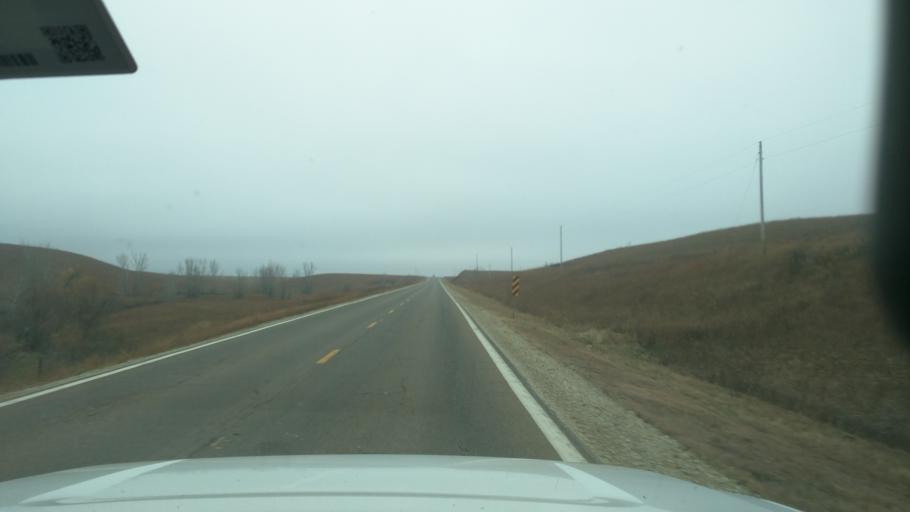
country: US
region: Kansas
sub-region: Riley County
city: Manhattan
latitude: 38.9928
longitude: -96.5199
